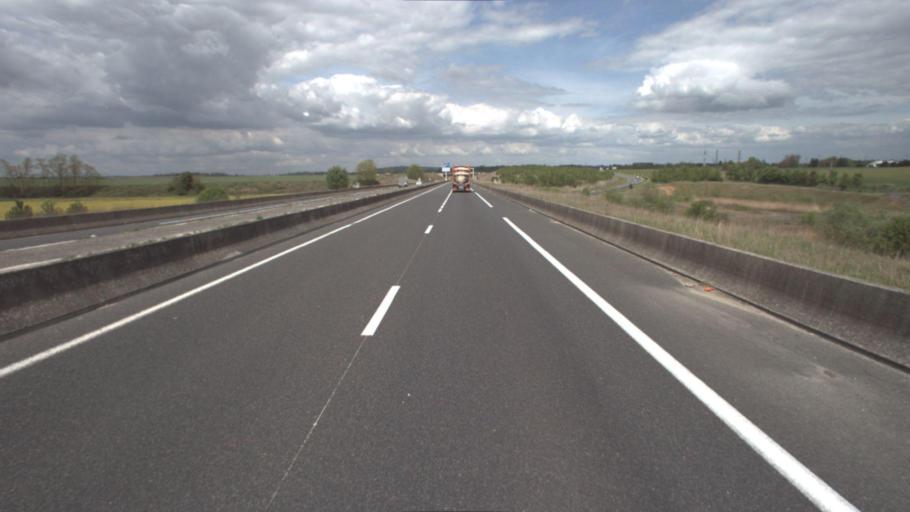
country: FR
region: Ile-de-France
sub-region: Departement de Seine-et-Marne
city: Villenoy
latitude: 48.9337
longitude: 2.8462
